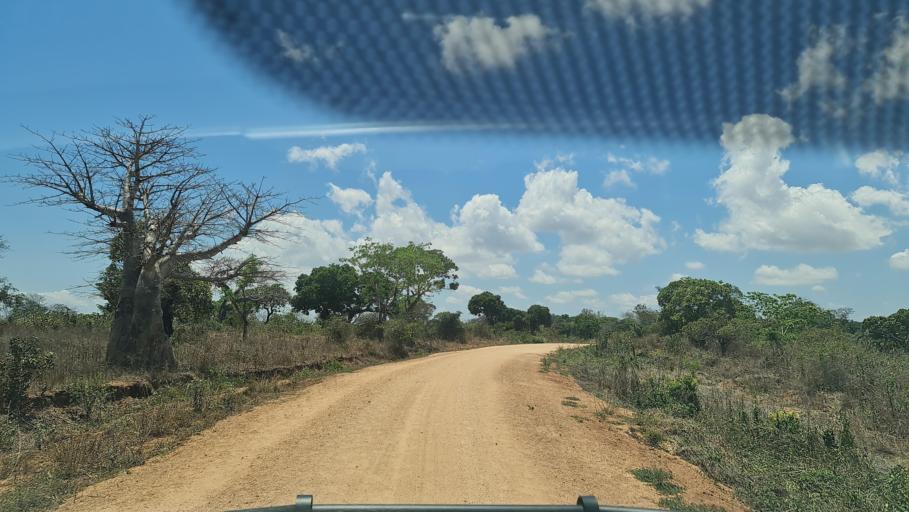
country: MZ
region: Nampula
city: Nacala
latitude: -14.3261
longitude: 40.5293
